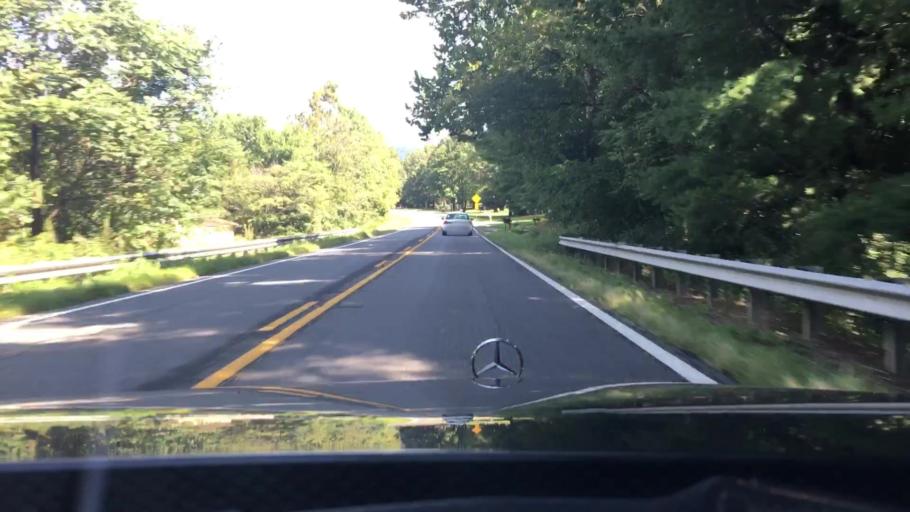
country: US
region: Virginia
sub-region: City of Waynesboro
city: Waynesboro
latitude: 38.0115
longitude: -78.8237
